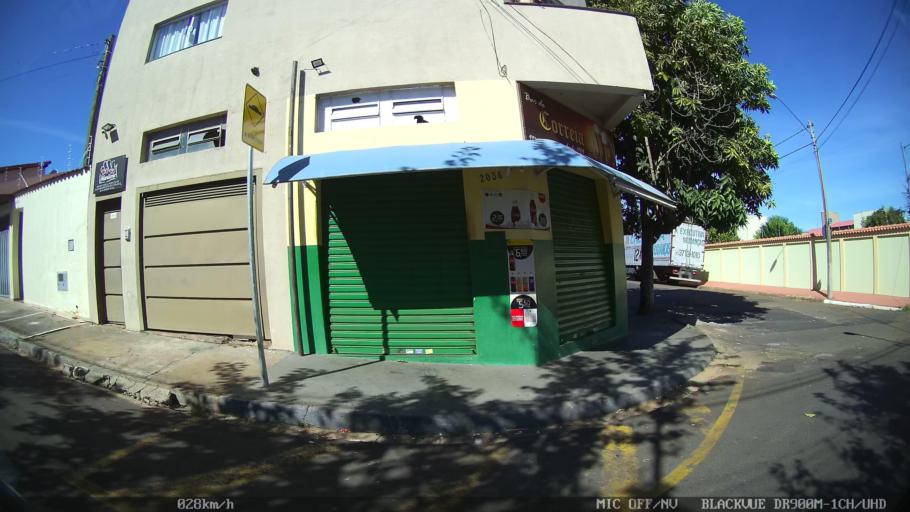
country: BR
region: Sao Paulo
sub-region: Franca
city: Franca
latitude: -20.5442
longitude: -47.3899
